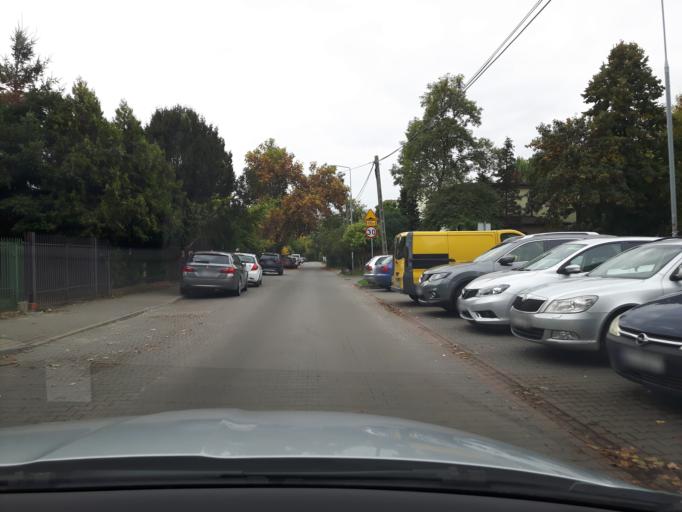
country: PL
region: Masovian Voivodeship
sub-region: Warszawa
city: Mokotow
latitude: 52.1763
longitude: 21.0179
